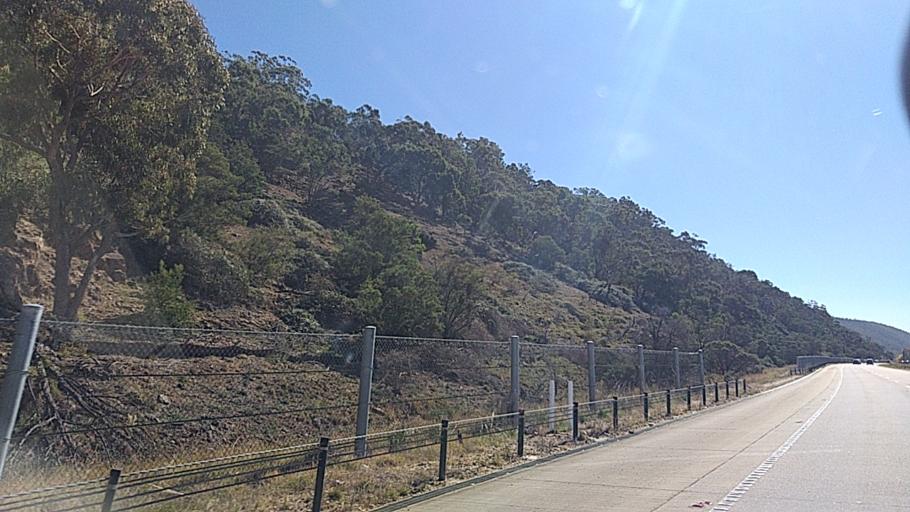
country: AU
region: New South Wales
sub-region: Yass Valley
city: Gundaroo
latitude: -35.0842
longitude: 149.3746
